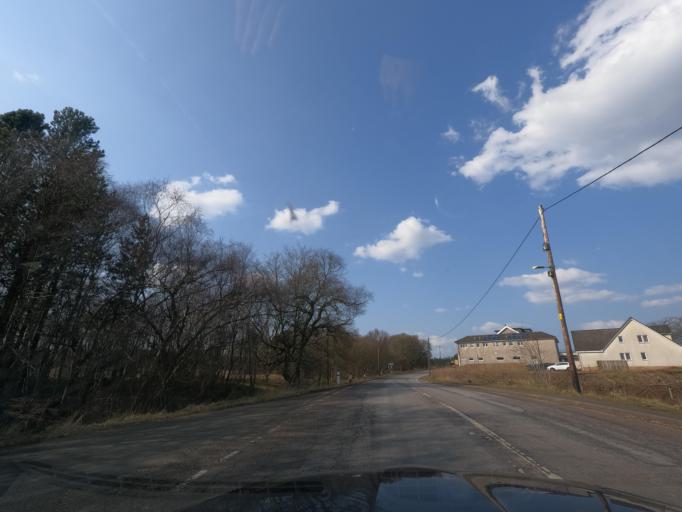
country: GB
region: Scotland
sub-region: South Lanarkshire
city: Forth
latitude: 55.7731
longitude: -3.6761
